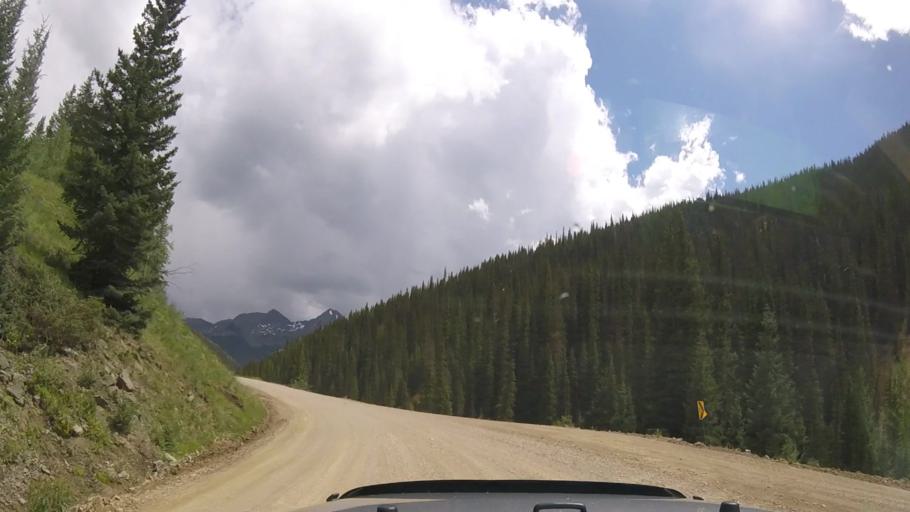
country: US
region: Colorado
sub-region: San Juan County
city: Silverton
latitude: 37.8355
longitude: -107.6774
